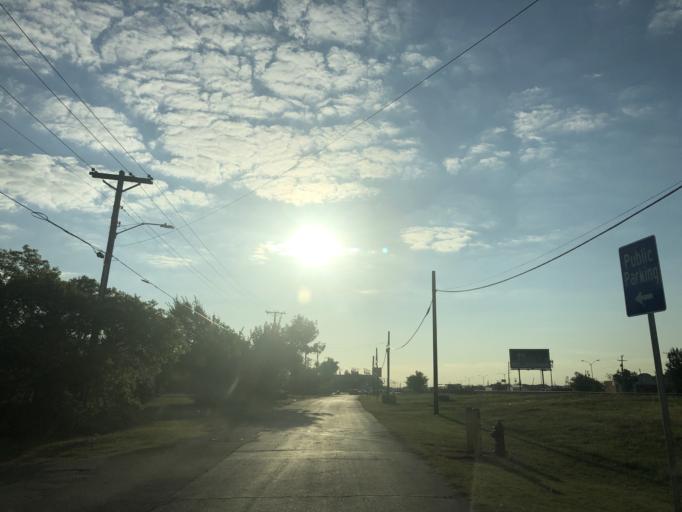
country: US
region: Texas
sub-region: Dallas County
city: Grand Prairie
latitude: 32.7445
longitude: -97.0092
